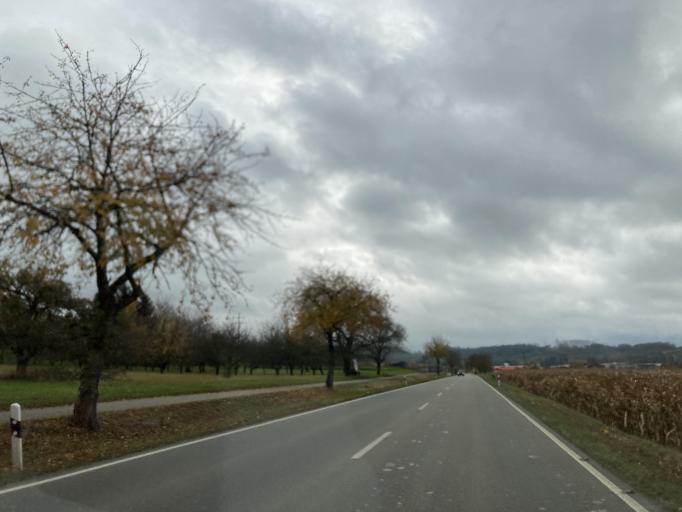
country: DE
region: Baden-Wuerttemberg
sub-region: Freiburg Region
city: Schliengen
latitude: 47.7695
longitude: 7.5797
